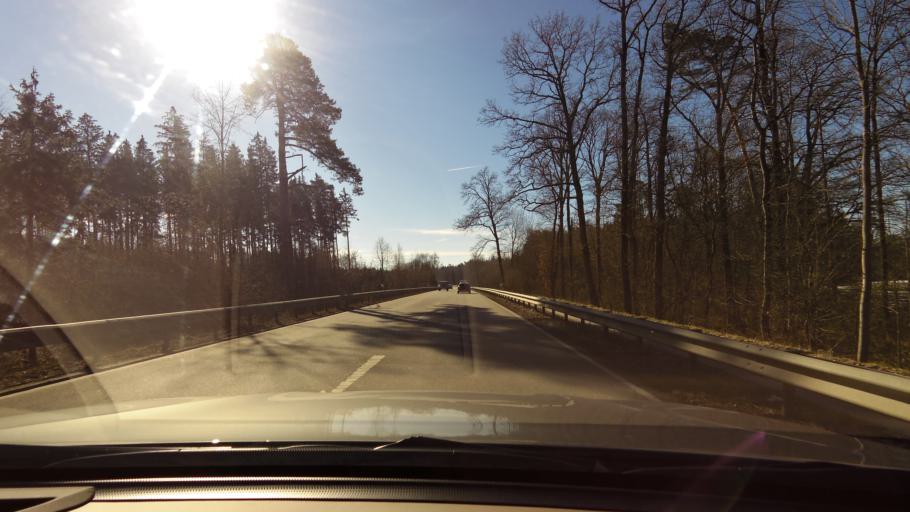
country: DE
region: Bavaria
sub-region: Upper Bavaria
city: Ampfing
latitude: 48.2318
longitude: 12.4141
